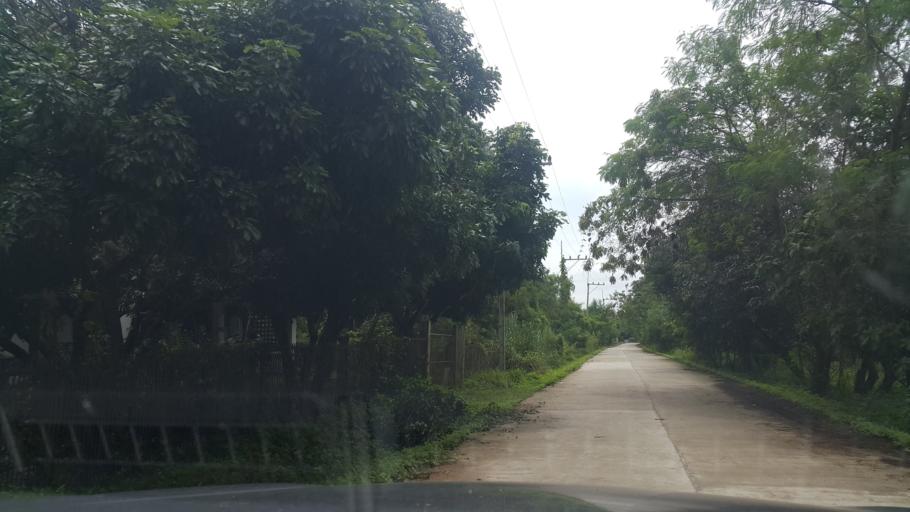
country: TH
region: Chiang Mai
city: San Sai
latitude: 18.9064
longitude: 99.0554
